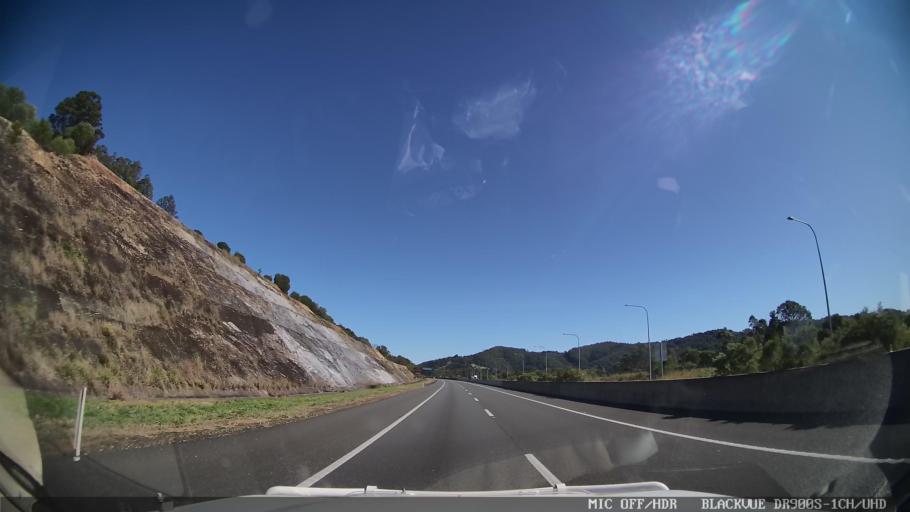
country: AU
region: Queensland
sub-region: Sunshine Coast
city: Black Mountain
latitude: -26.3912
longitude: 152.8101
